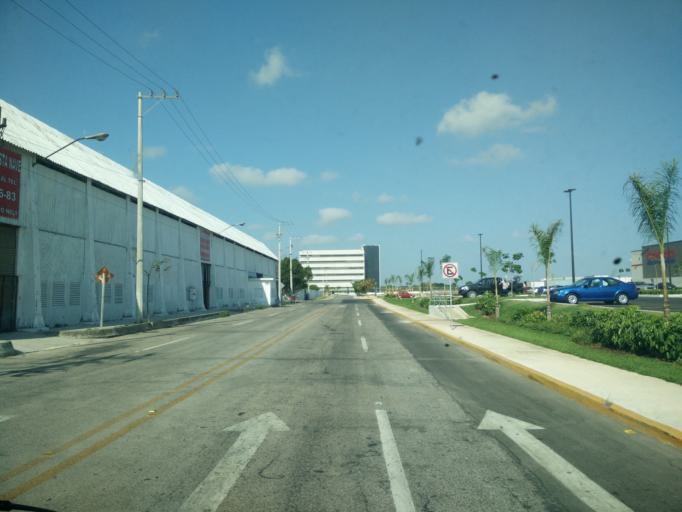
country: MX
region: Yucatan
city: Merida
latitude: 21.0366
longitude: -89.6291
